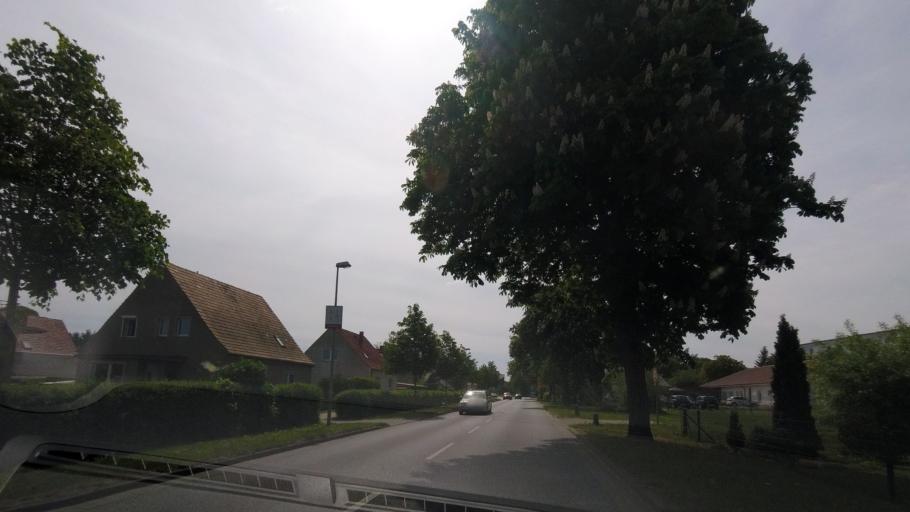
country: DE
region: Brandenburg
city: Wittstock
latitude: 53.1543
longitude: 12.4842
